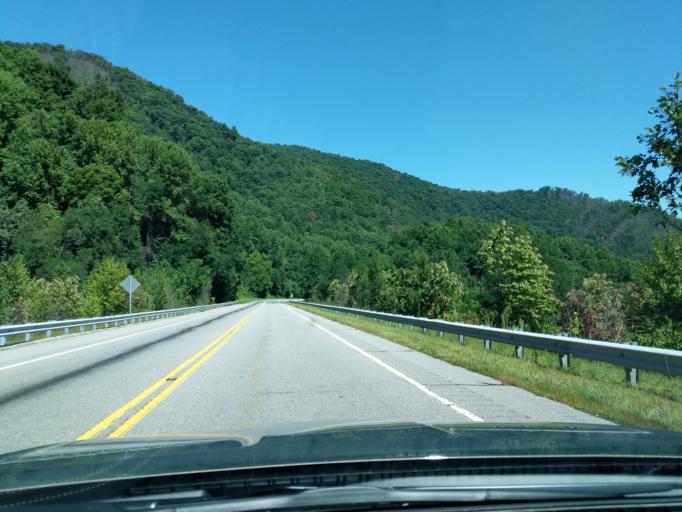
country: US
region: North Carolina
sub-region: Macon County
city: Franklin
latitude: 35.1257
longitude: -83.5397
